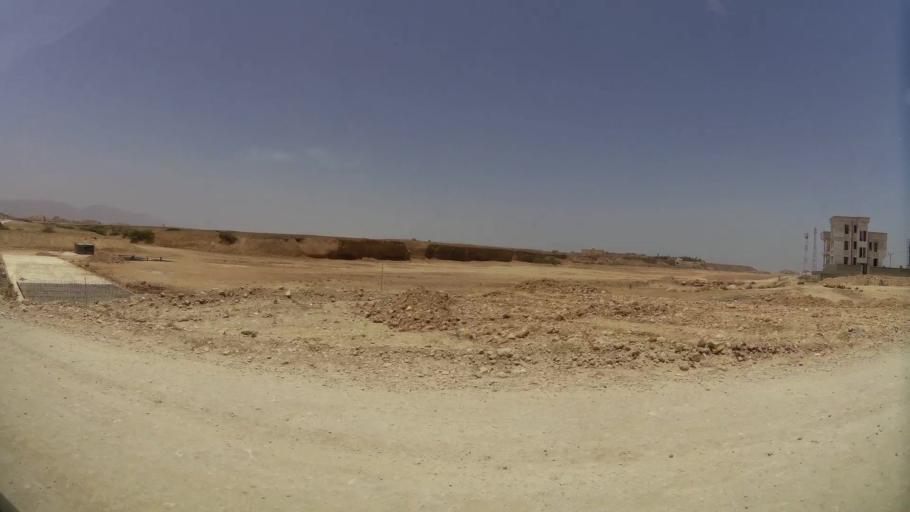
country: OM
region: Zufar
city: Salalah
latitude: 17.0890
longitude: 54.1620
